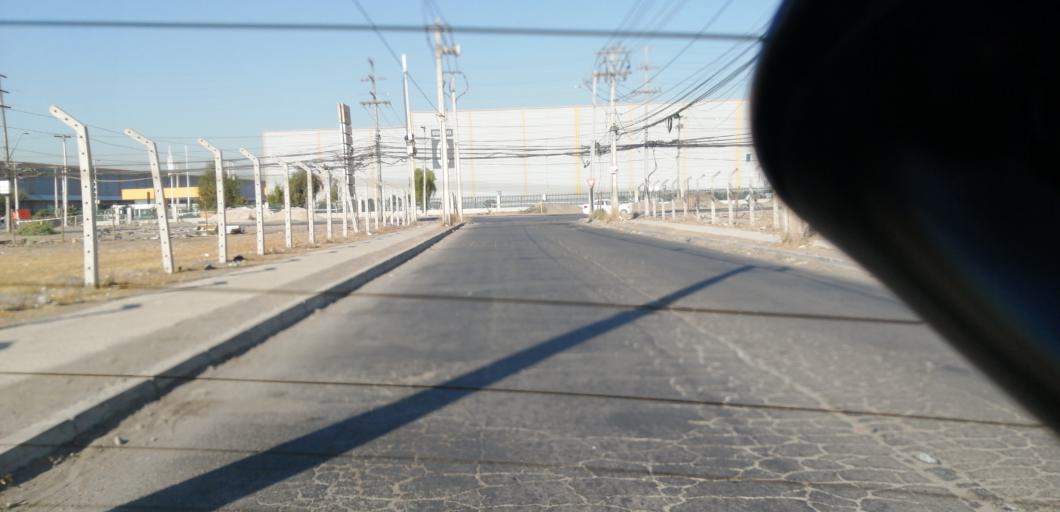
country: CL
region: Santiago Metropolitan
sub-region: Provincia de Santiago
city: Lo Prado
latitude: -33.3817
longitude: -70.7669
